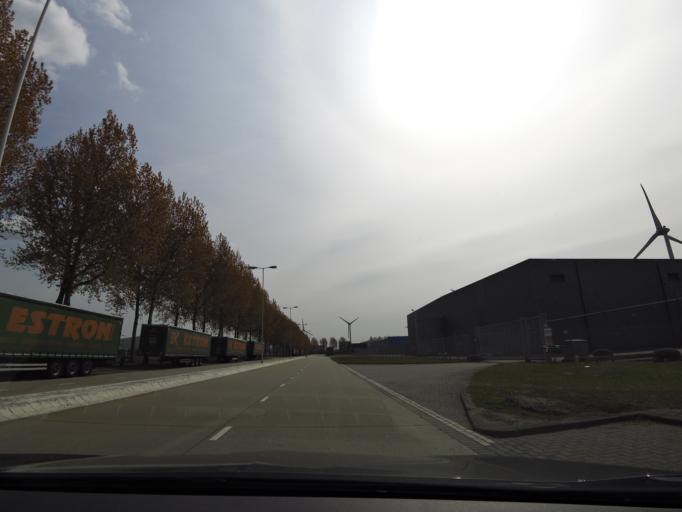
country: NL
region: South Holland
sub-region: Gemeente Maassluis
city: Maassluis
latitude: 51.8724
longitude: 4.2558
